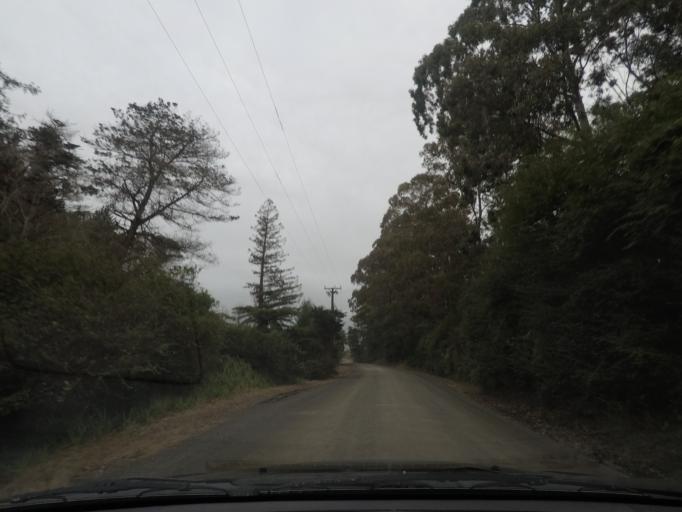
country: NZ
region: Auckland
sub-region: Auckland
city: Muriwai Beach
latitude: -36.7546
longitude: 174.5752
